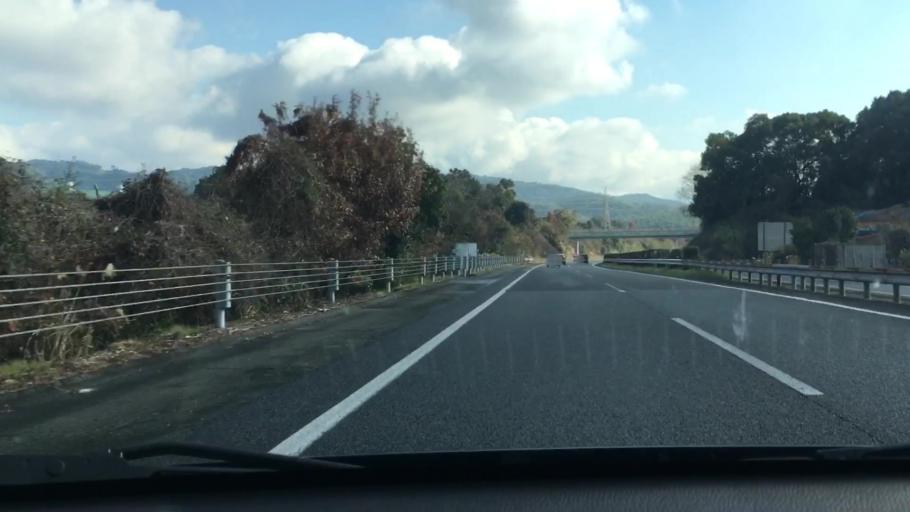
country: JP
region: Kumamoto
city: Matsubase
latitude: 32.6391
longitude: 130.7081
